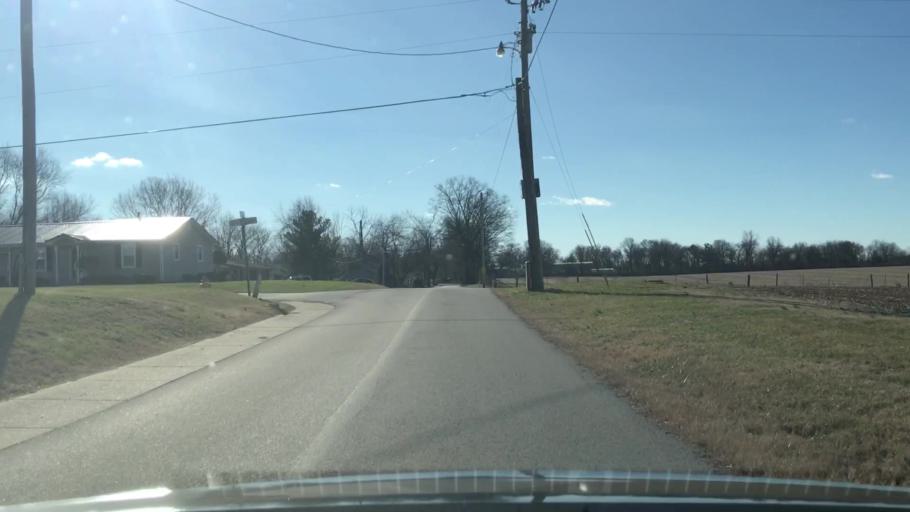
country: US
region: Kentucky
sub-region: Edmonson County
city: Brownsville
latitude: 37.0555
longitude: -86.2110
